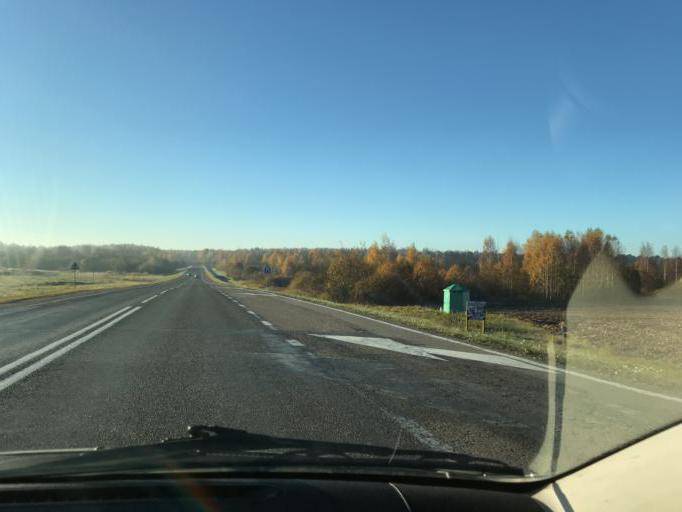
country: BY
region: Vitebsk
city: Vitebsk
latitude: 54.9079
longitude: 30.3760
